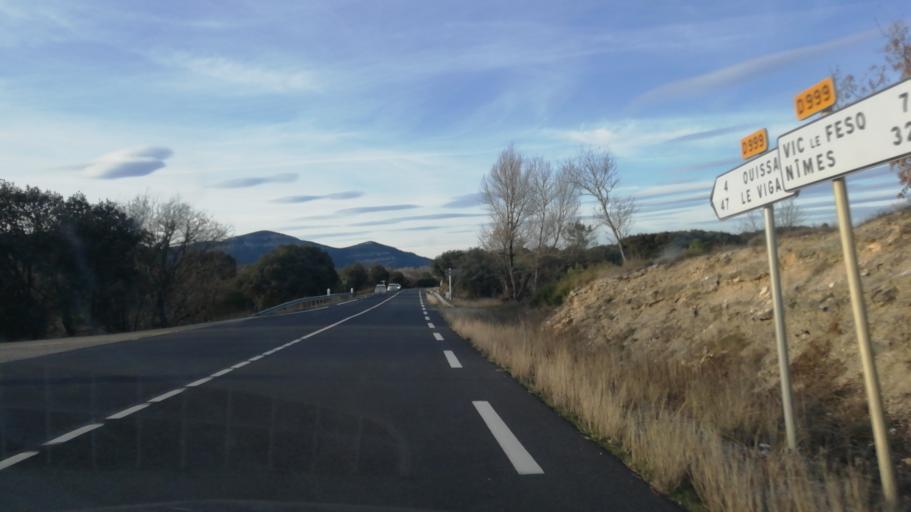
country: FR
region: Languedoc-Roussillon
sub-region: Departement du Gard
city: Quissac
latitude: 43.8869
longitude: 4.0165
